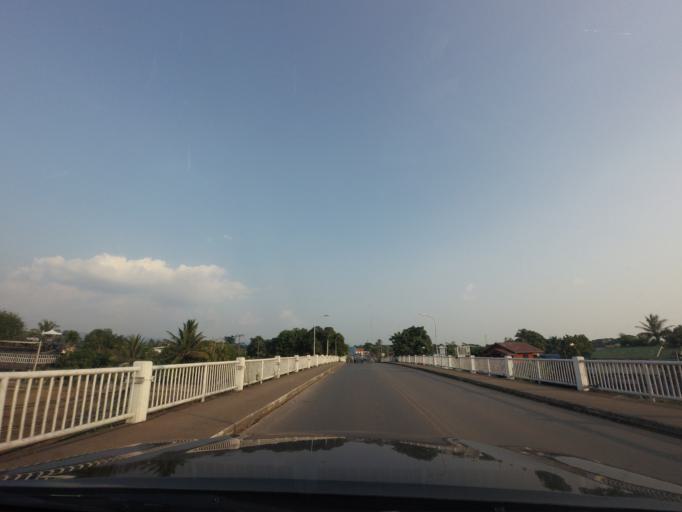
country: TH
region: Nan
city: Nan
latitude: 18.7749
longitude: 100.7797
